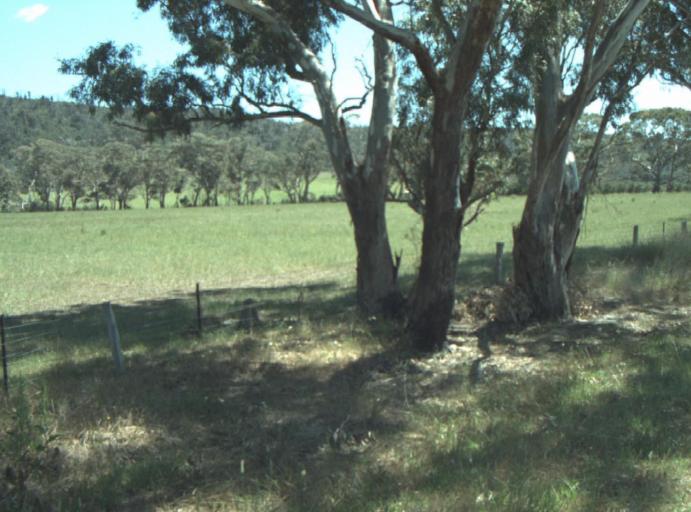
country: AU
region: Victoria
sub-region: Greater Geelong
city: Lara
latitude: -37.8624
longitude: 144.2794
